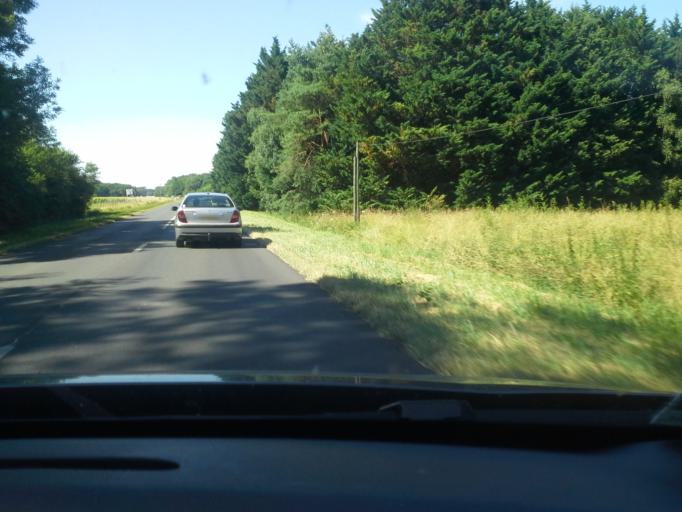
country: FR
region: Centre
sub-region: Departement du Loir-et-Cher
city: Cormeray
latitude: 47.5015
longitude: 1.4055
